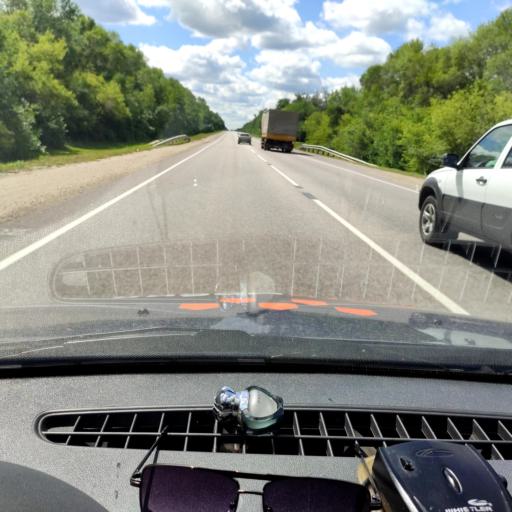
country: RU
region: Lipetsk
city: Borinskoye
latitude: 52.3849
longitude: 39.2228
